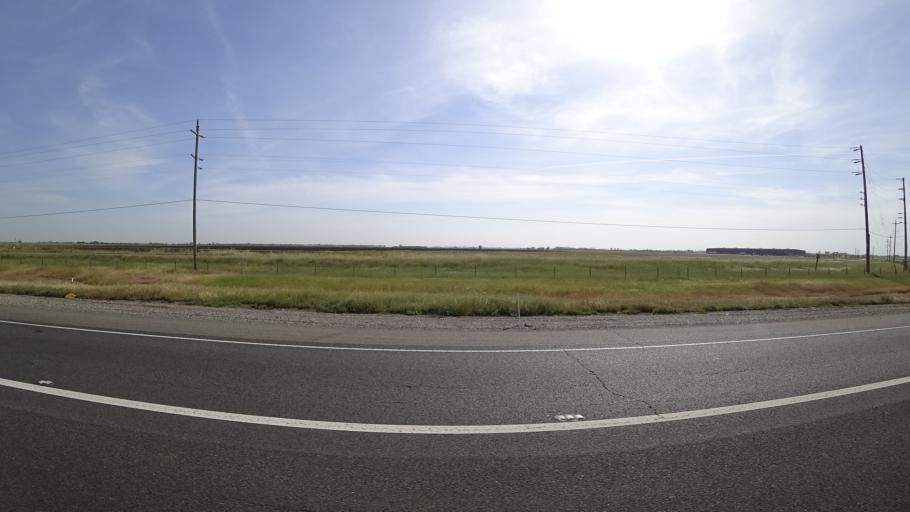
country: US
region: California
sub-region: Butte County
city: Durham
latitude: 39.6402
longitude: -121.7139
